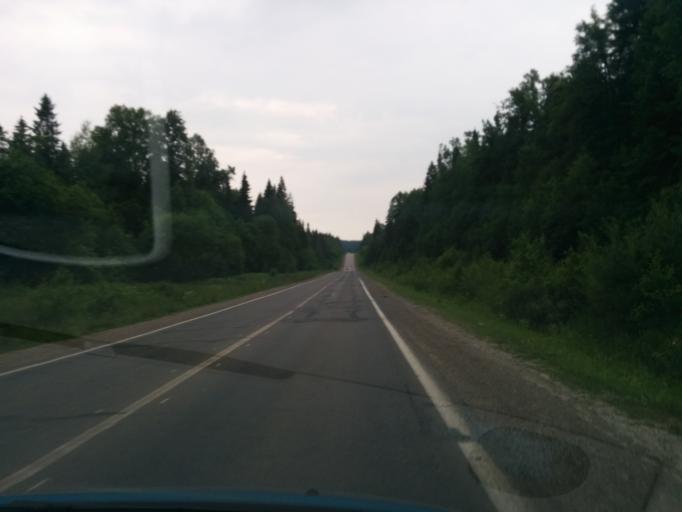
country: RU
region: Perm
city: Perm
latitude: 58.1884
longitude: 56.2175
